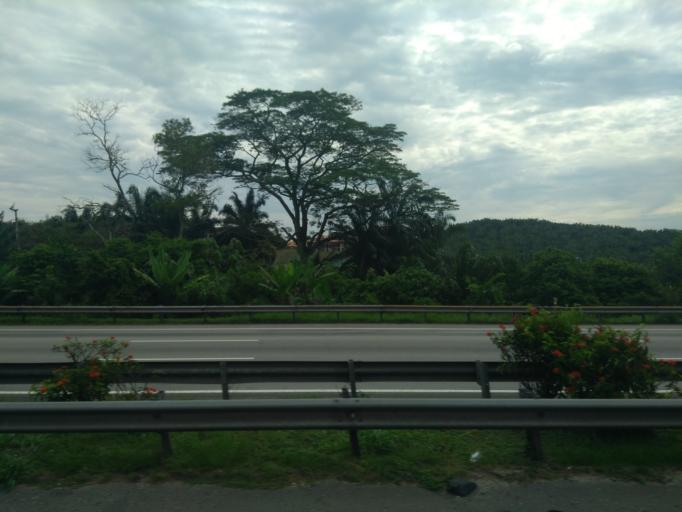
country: MY
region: Negeri Sembilan
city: Seremban
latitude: 2.6484
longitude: 101.9921
